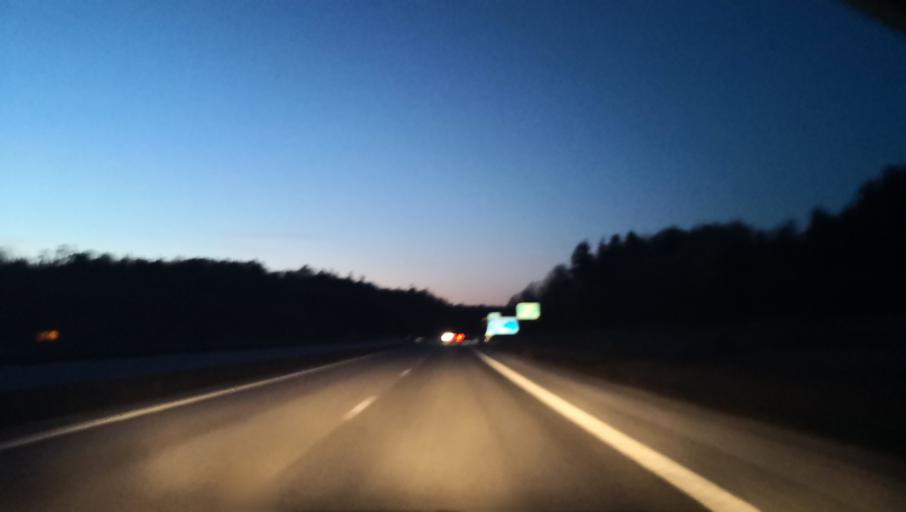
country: SE
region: Stockholm
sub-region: Nynashamns Kommun
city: Osmo
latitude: 58.9654
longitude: 17.9072
